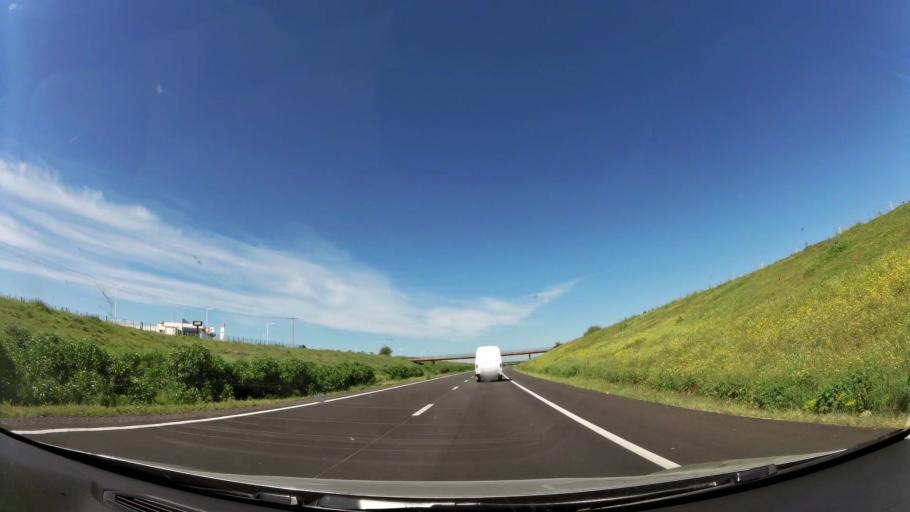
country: MA
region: Meknes-Tafilalet
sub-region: Meknes
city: Meknes
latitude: 33.8340
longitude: -5.4690
